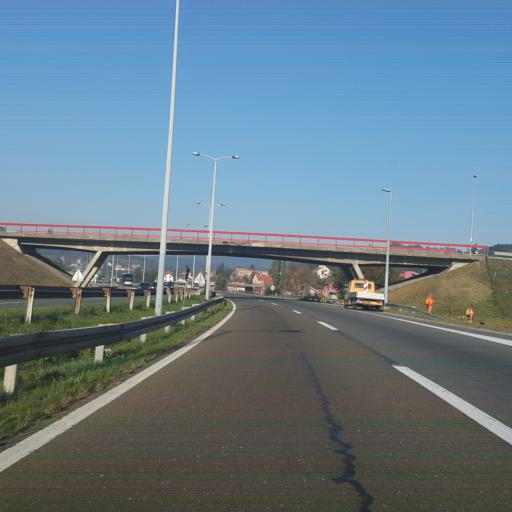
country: RS
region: Central Serbia
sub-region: Belgrade
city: Grocka
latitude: 44.6735
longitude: 20.6024
